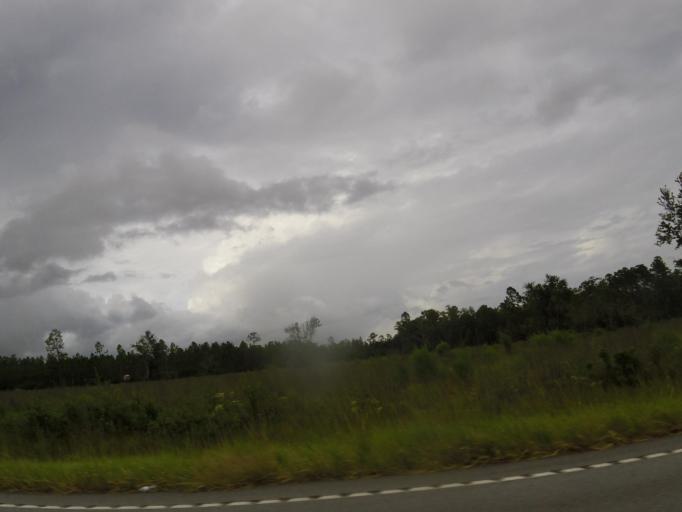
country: US
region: Florida
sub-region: Nassau County
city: Hilliard
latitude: 30.5221
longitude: -82.0749
